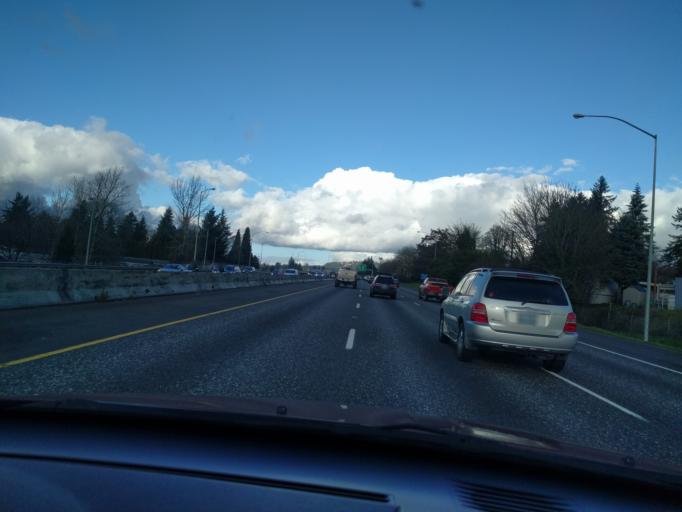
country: US
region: Oregon
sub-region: Clackamas County
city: Clackamas
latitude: 45.4016
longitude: -122.5728
